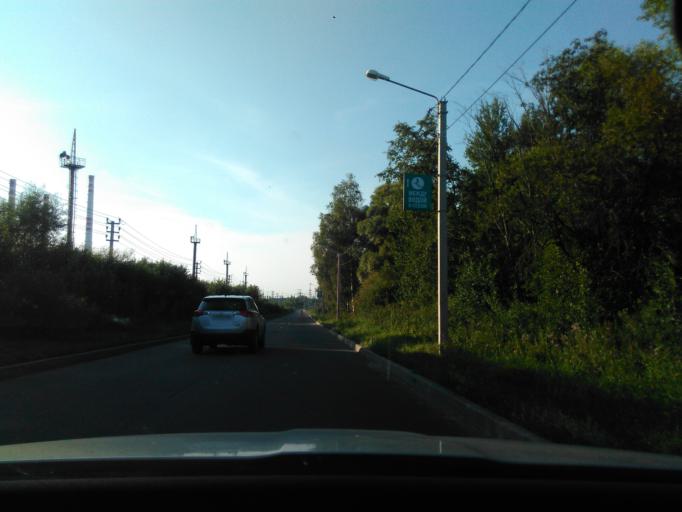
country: RU
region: Tverskaya
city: Konakovo
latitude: 56.7336
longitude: 36.7834
